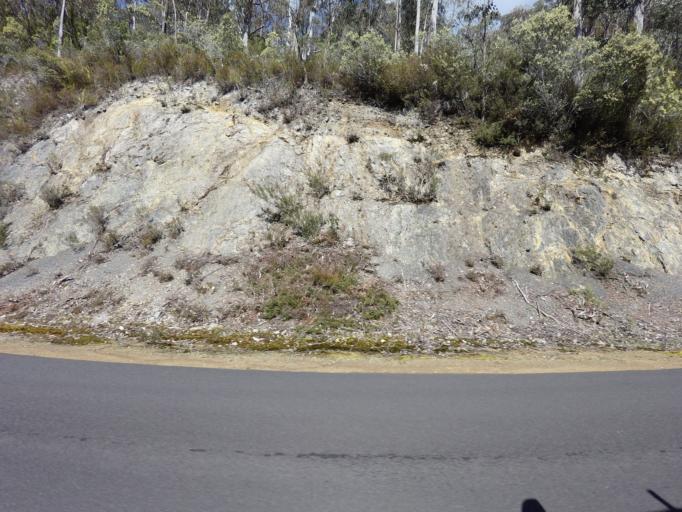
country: AU
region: Tasmania
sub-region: Derwent Valley
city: New Norfolk
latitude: -42.7284
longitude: 146.4659
